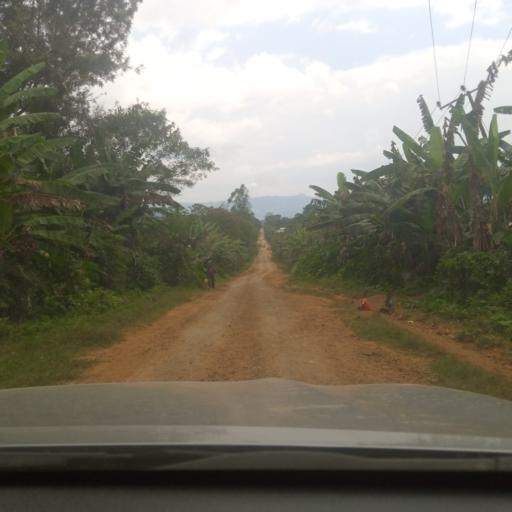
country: ET
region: Southern Nations, Nationalities, and People's Region
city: Tippi
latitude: 7.1393
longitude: 35.4205
